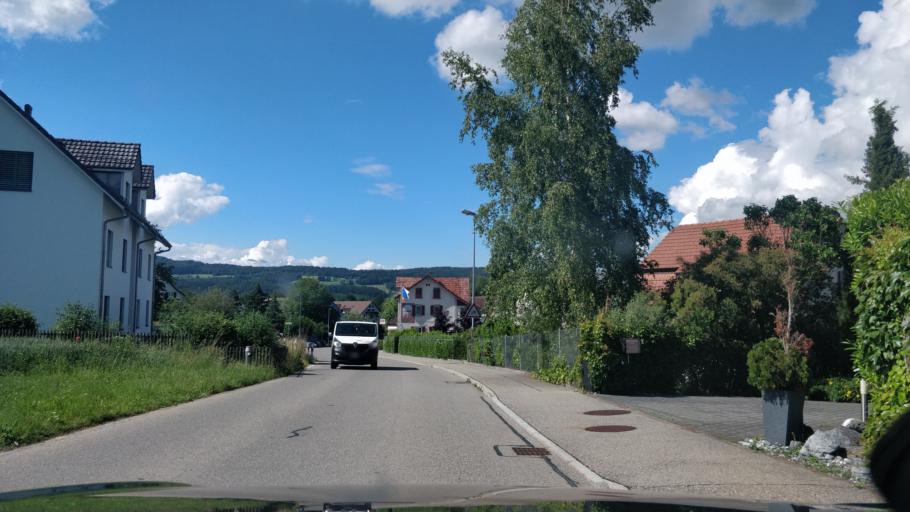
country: CH
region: Zurich
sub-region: Bezirk Buelach
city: Glattfelden
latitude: 47.5686
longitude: 8.4721
